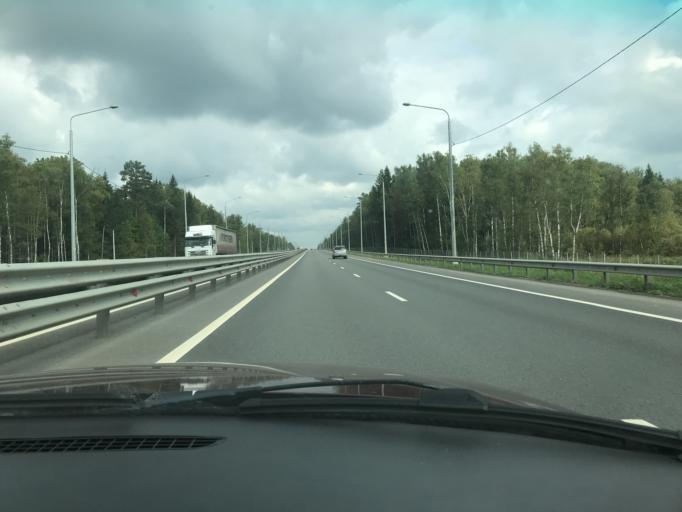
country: RU
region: Kaluga
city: Pyatovskiy
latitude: 54.6606
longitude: 36.1417
